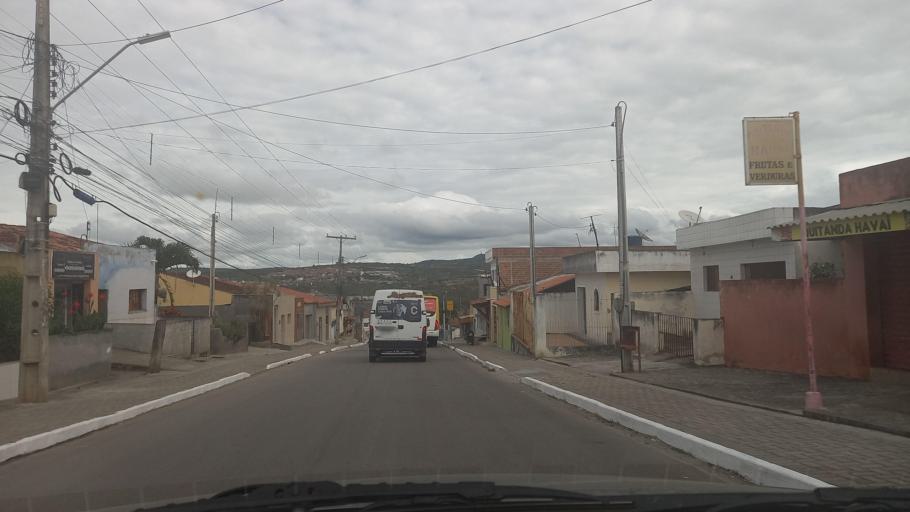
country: BR
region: Pernambuco
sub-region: Caruaru
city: Caruaru
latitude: -8.2943
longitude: -36.0303
